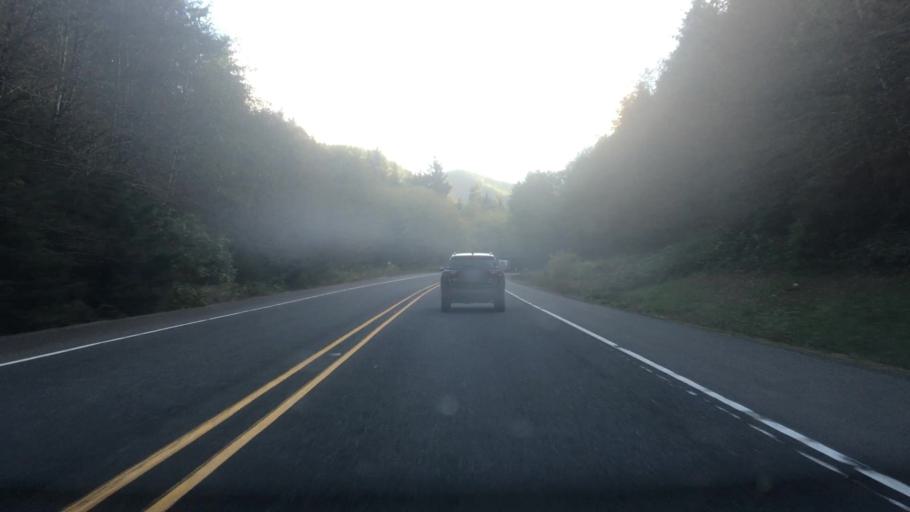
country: US
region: Oregon
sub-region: Clatsop County
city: Cannon Beach
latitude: 45.9319
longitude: -123.9276
